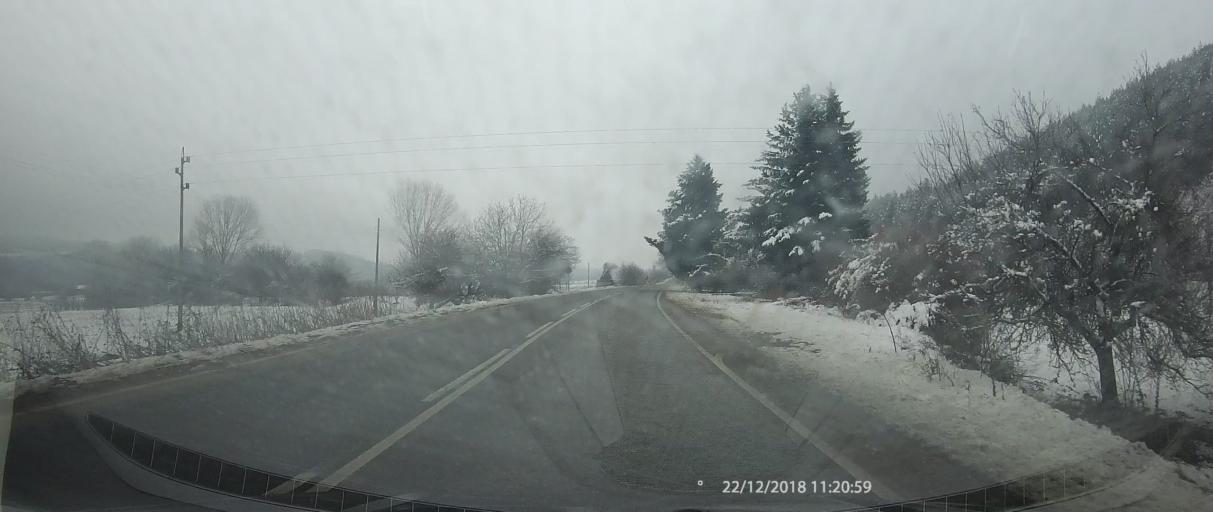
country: BG
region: Kyustendil
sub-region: Obshtina Kyustendil
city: Kyustendil
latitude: 42.2608
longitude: 22.8310
